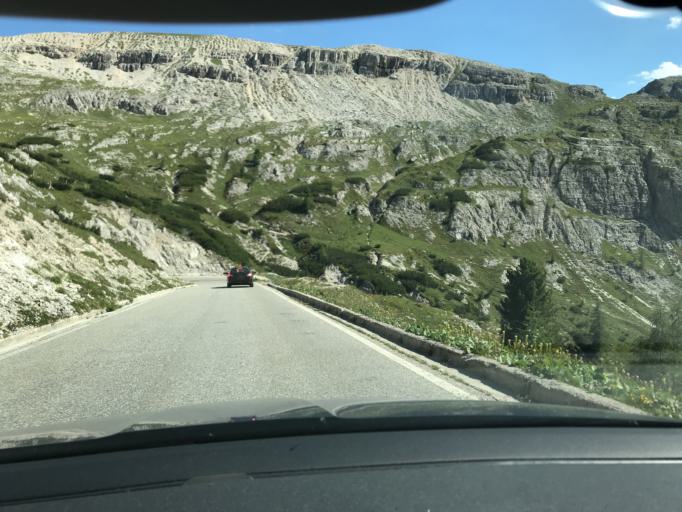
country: IT
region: Trentino-Alto Adige
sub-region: Bolzano
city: Sesto
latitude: 46.6074
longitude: 12.2943
